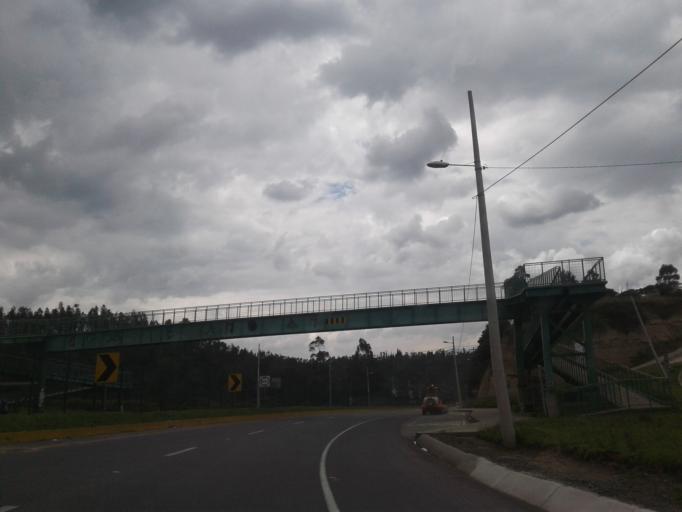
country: EC
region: Pichincha
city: Sangolqui
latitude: -0.3215
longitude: -78.3716
